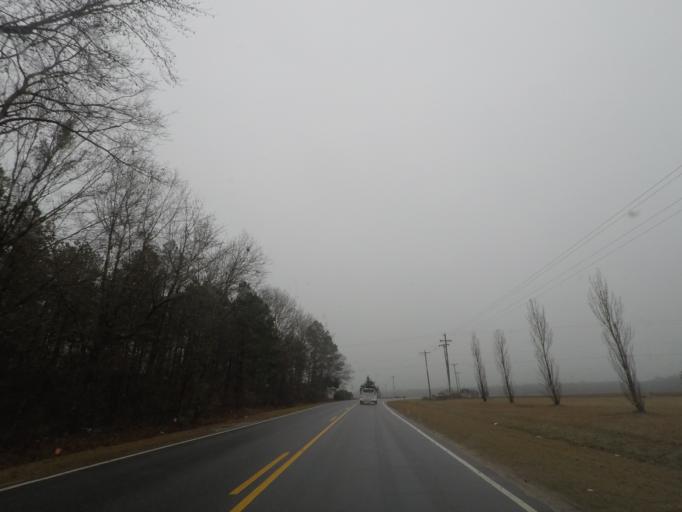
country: US
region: North Carolina
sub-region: Scotland County
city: Laurinburg
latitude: 34.7974
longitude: -79.4299
